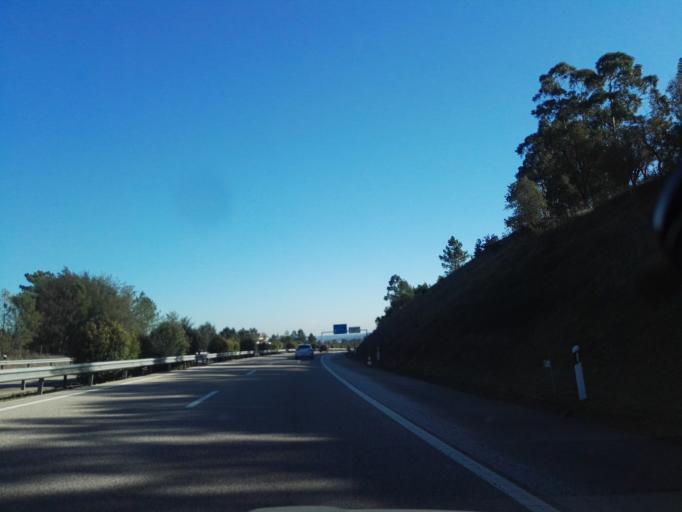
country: PT
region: Santarem
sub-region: Constancia
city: Constancia
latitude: 39.4855
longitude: -8.3599
